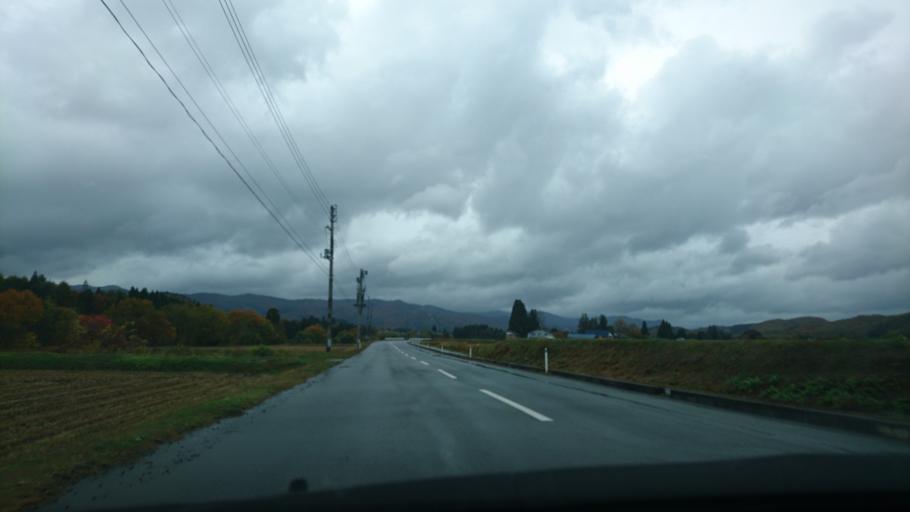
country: JP
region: Akita
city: Yokotemachi
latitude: 39.3835
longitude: 140.7659
